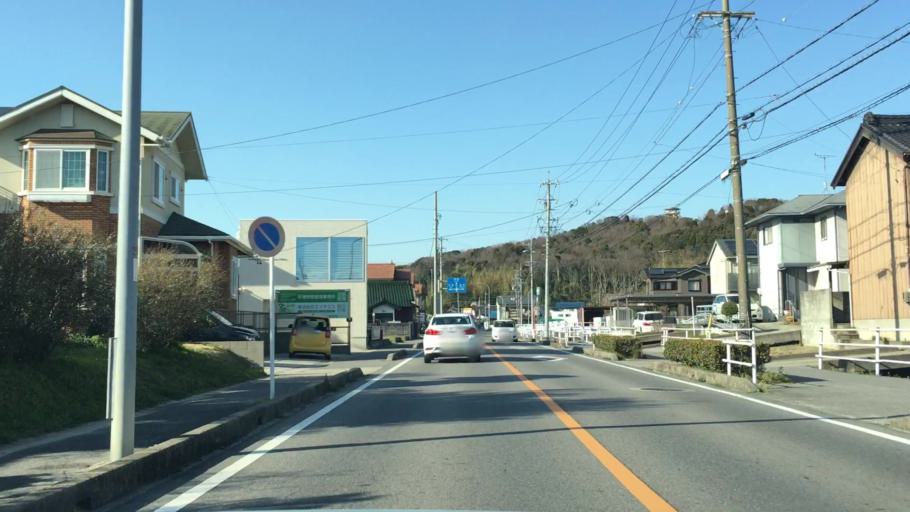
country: JP
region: Aichi
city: Nishio
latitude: 34.8701
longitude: 137.0740
